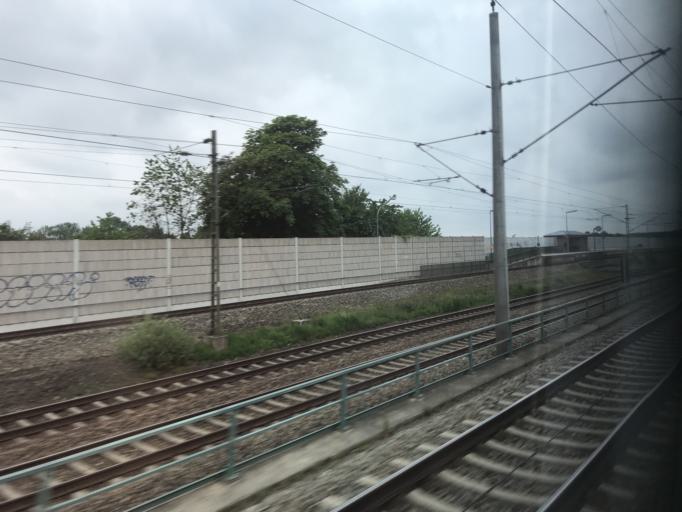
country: DE
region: Bavaria
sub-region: Upper Bavaria
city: Maisach
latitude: 48.2154
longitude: 11.2216
